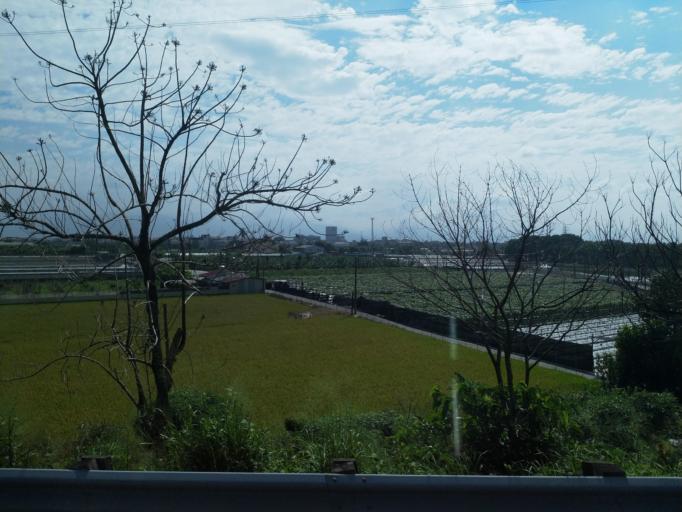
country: TW
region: Taiwan
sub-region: Pingtung
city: Pingtung
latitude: 22.8094
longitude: 120.4842
